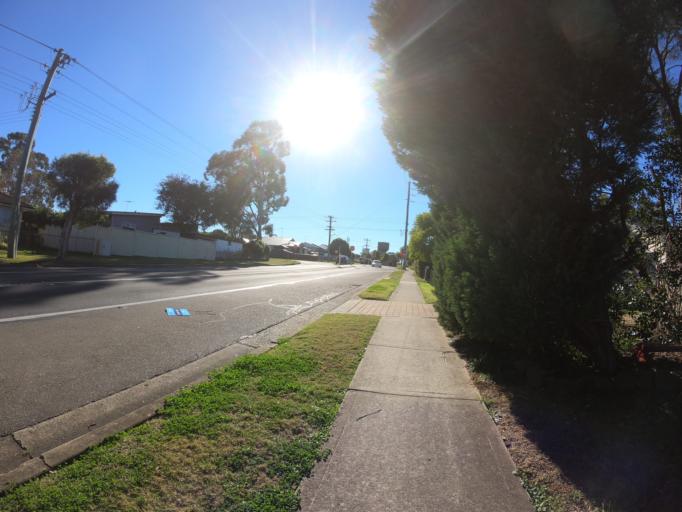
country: AU
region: New South Wales
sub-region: Hawkesbury
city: South Windsor
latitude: -33.6280
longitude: 150.7993
